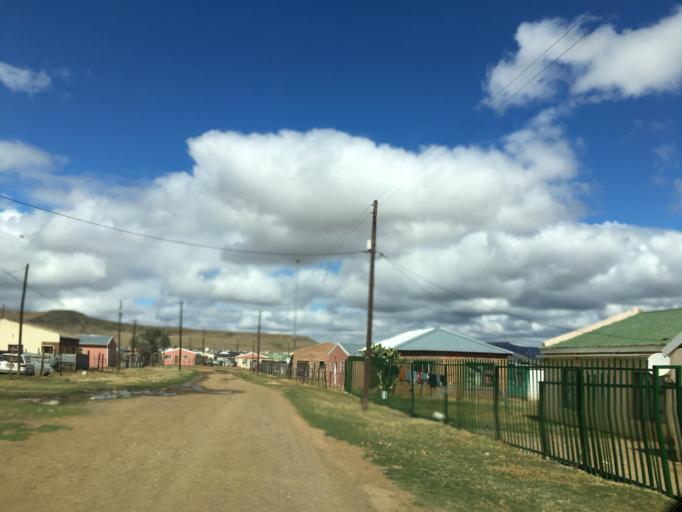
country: ZA
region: Eastern Cape
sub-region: Chris Hani District Municipality
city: Cala
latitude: -31.5339
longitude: 27.7023
